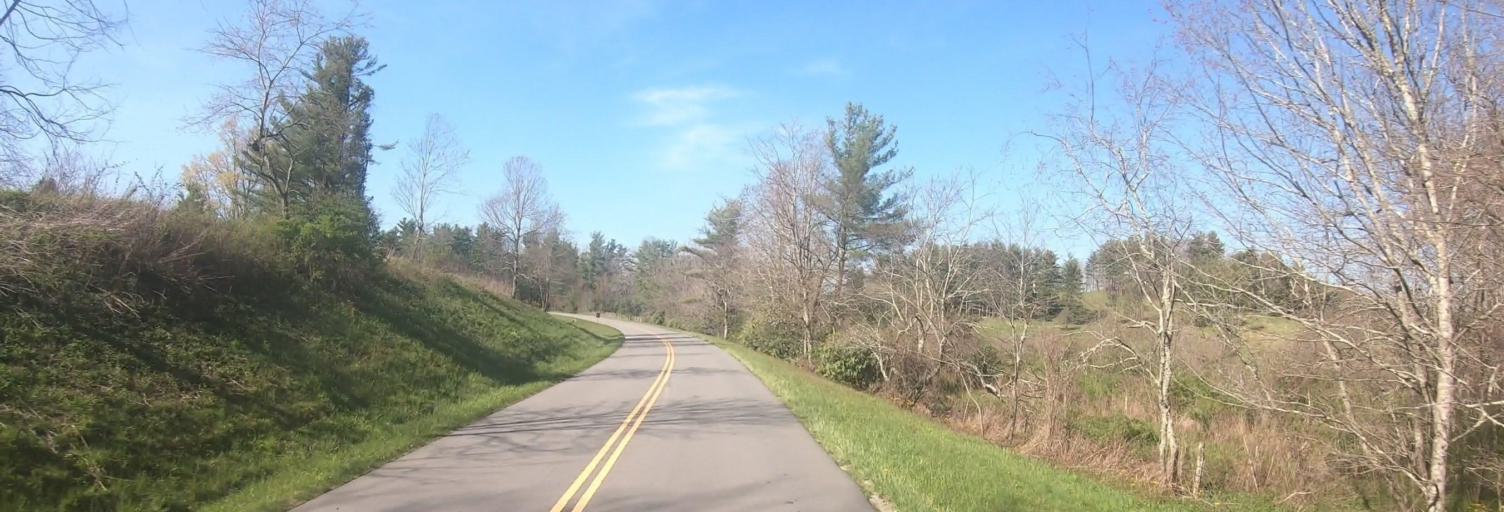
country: US
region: North Carolina
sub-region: Watauga County
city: Boone
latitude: 36.1880
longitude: -81.6034
